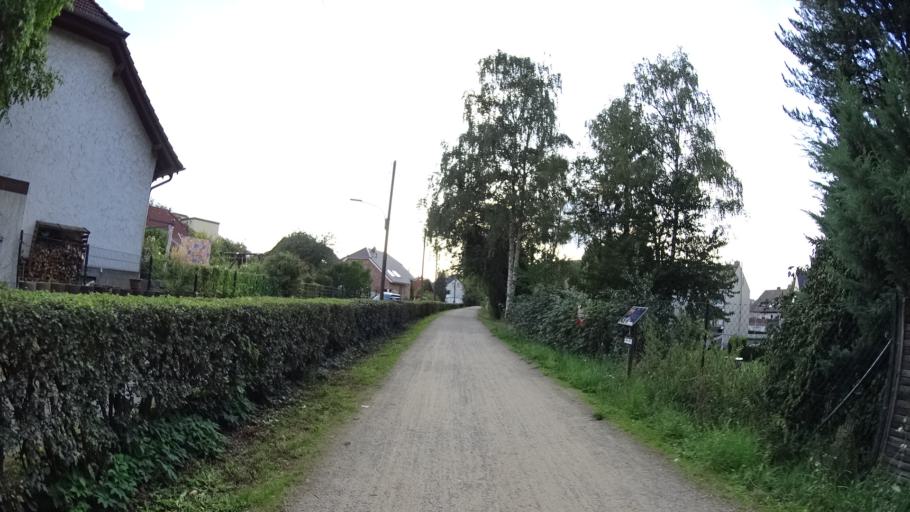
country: DE
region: North Rhine-Westphalia
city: Witten
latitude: 51.4507
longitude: 7.4027
